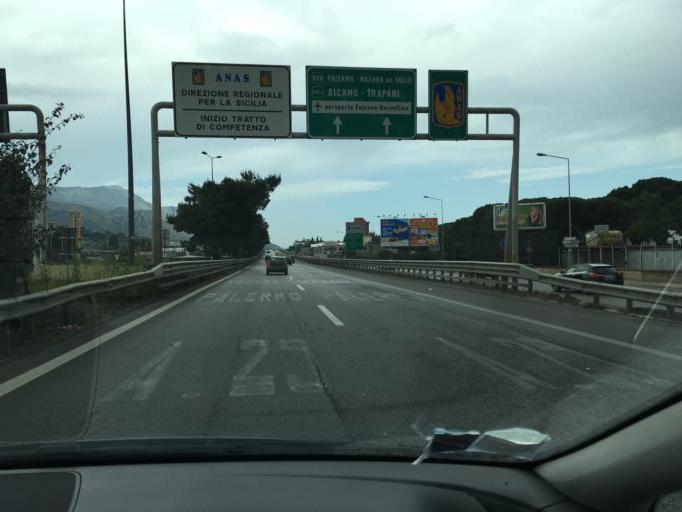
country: IT
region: Sicily
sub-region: Palermo
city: Palermo
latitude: 38.1521
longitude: 13.3222
